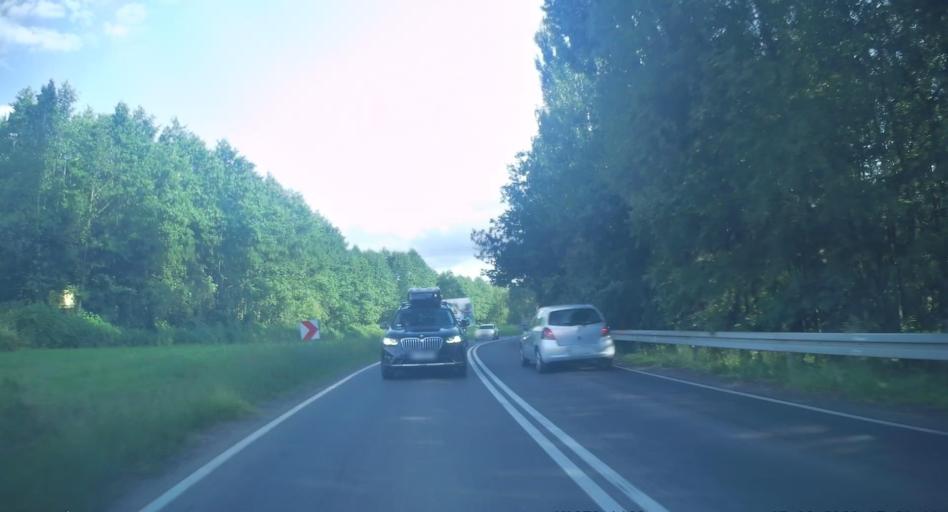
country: PL
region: Lesser Poland Voivodeship
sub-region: Powiat oswiecimski
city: Grojec
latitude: 49.9765
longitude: 19.2221
